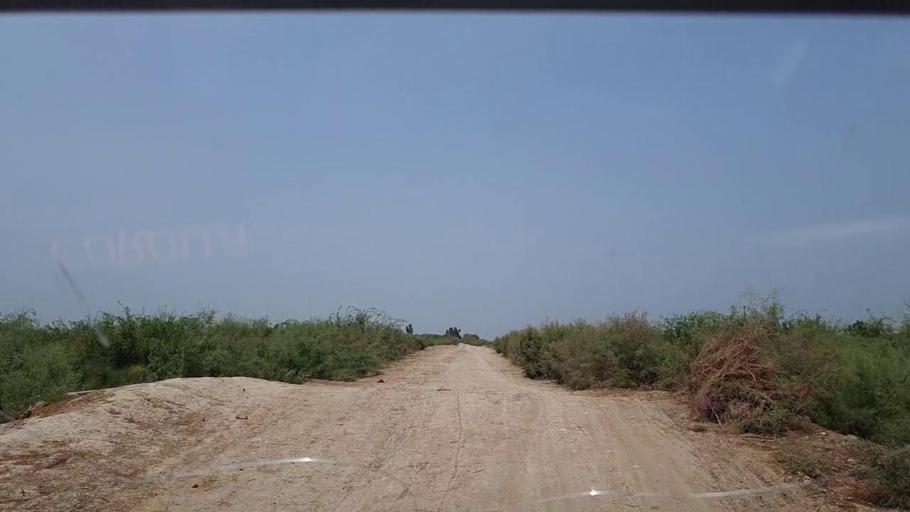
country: PK
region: Sindh
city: Adilpur
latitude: 27.8998
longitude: 69.2339
